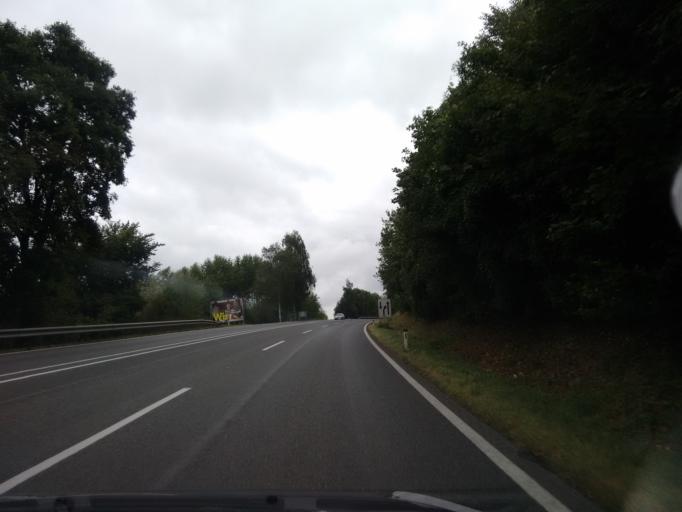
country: AT
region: Upper Austria
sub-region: Politischer Bezirk Grieskirchen
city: Bad Schallerbach
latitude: 48.2198
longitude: 13.9027
